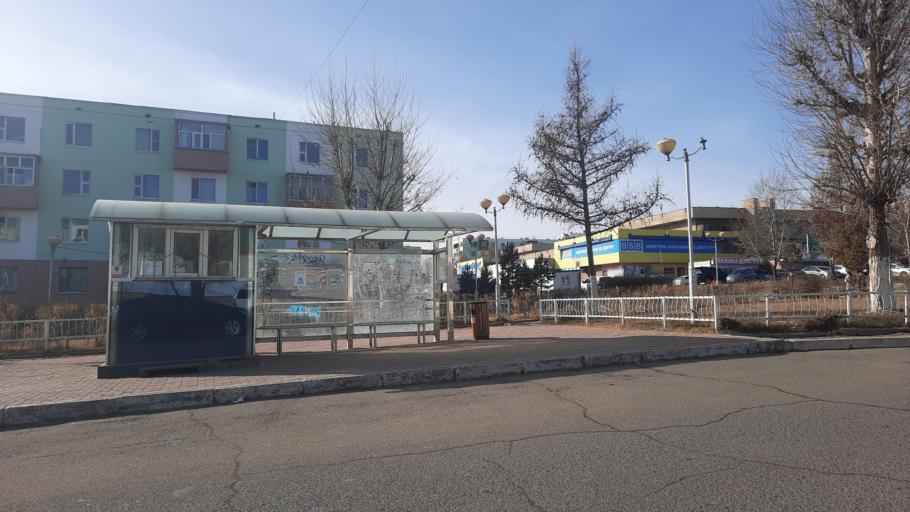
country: MN
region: Orhon
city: Erdenet
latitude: 49.0292
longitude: 104.0569
